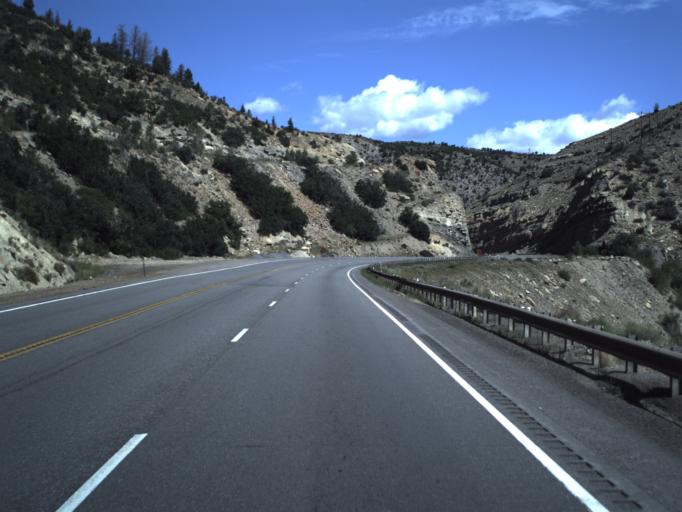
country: US
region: Utah
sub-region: Carbon County
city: Helper
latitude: 39.7947
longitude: -110.9319
